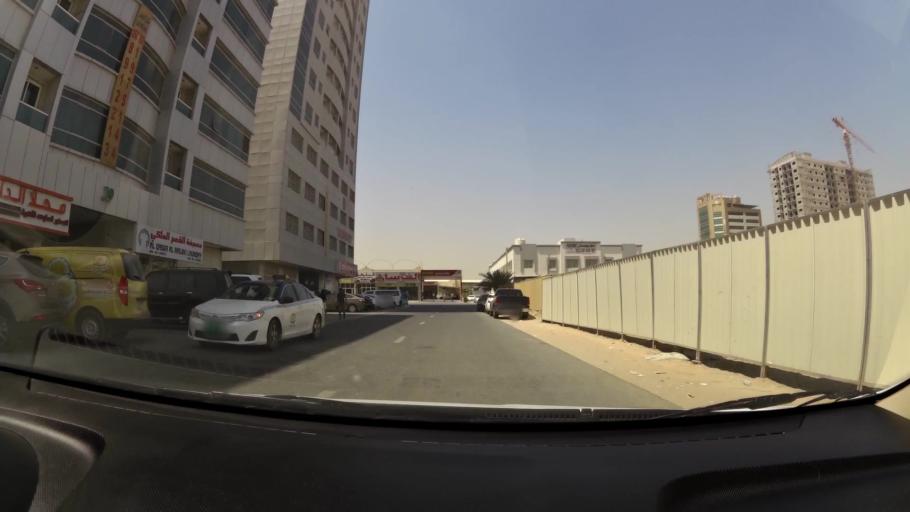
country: AE
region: Ajman
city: Ajman
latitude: 25.4028
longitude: 55.5066
